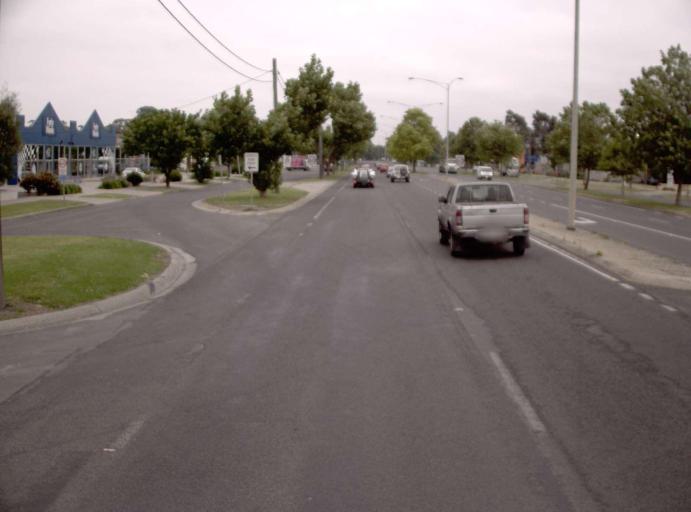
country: AU
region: Victoria
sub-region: Latrobe
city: Traralgon
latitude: -38.1927
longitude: 146.5500
